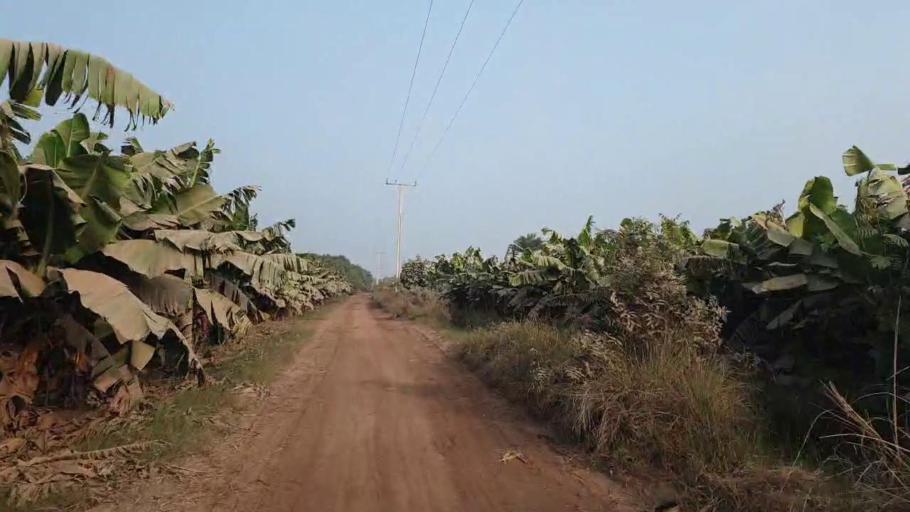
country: PK
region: Sindh
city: Tando Muhammad Khan
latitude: 25.1554
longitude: 68.5862
